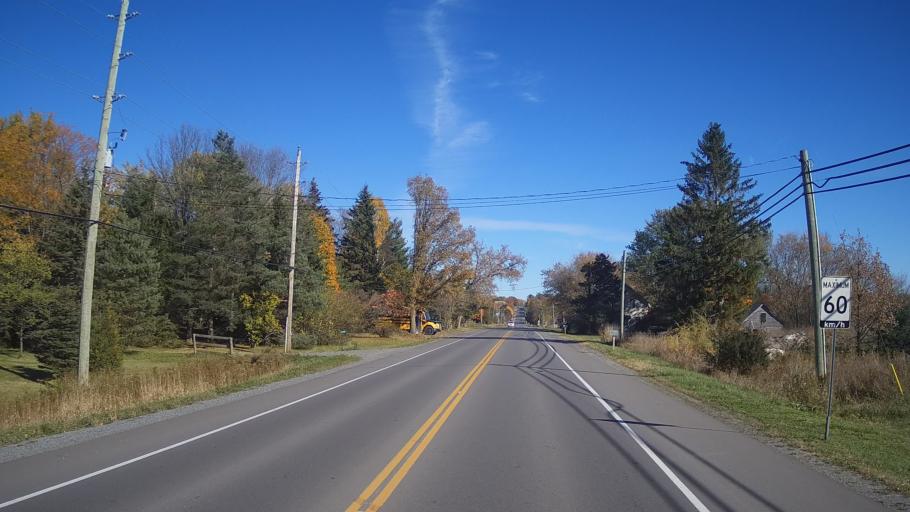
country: CA
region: Ontario
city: Kingston
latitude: 44.4065
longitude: -76.6105
